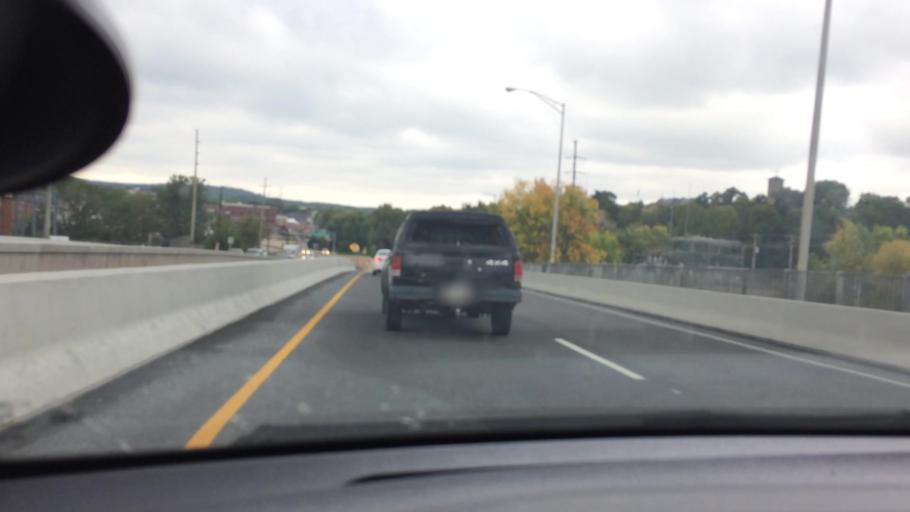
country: US
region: Wisconsin
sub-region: Chippewa County
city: Chippewa Falls
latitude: 44.9315
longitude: -91.3873
